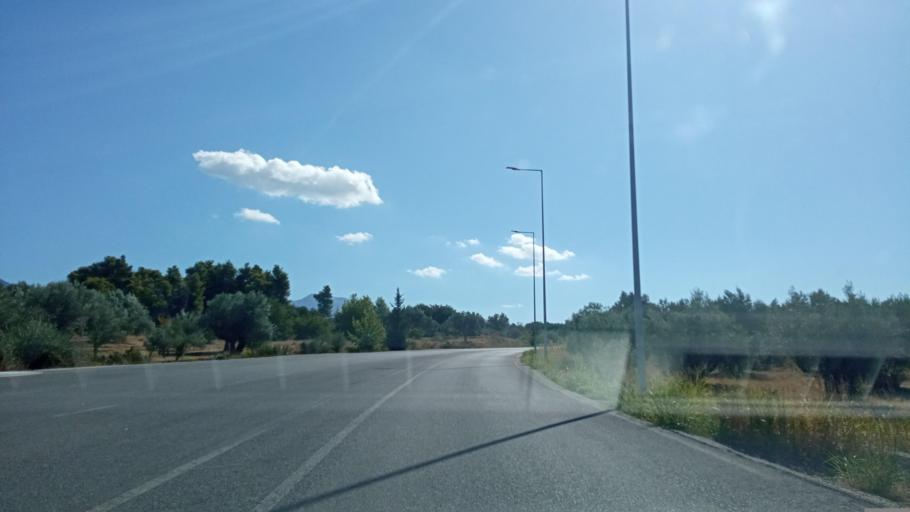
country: GR
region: Central Greece
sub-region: Nomos Evvoias
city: Psachna
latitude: 38.5798
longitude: 23.7694
